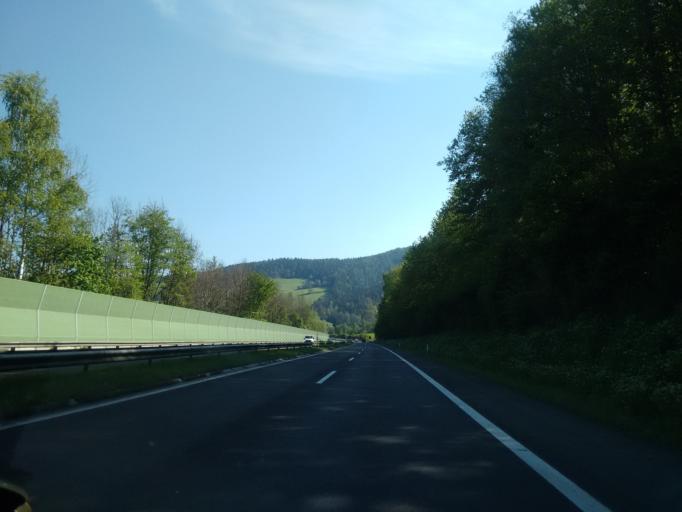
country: AT
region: Styria
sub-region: Politischer Bezirk Leoben
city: Leoben
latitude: 47.3576
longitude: 15.1031
